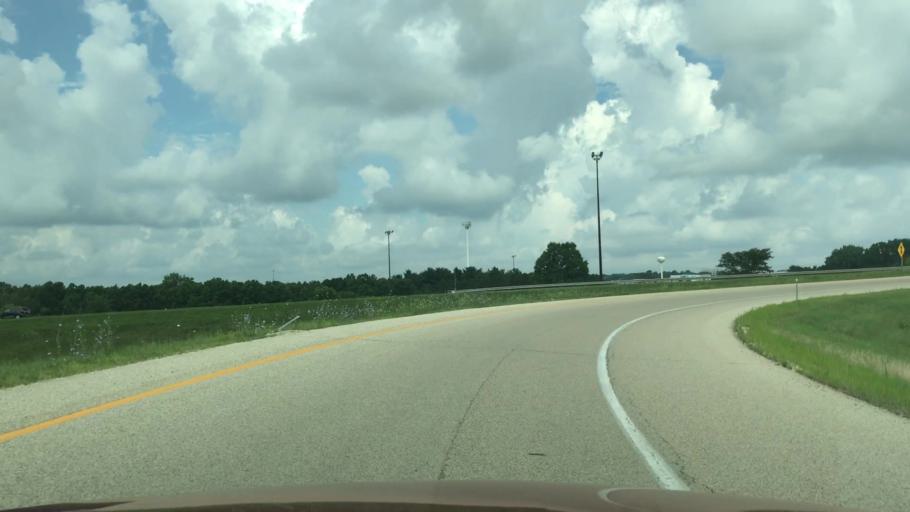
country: US
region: Illinois
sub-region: Winnebago County
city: Cherry Valley
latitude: 42.2375
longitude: -88.9658
